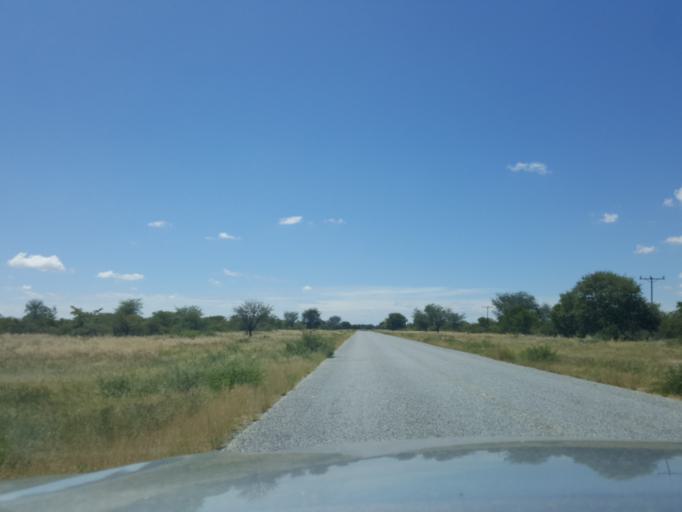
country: BW
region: Central
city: Nata
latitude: -20.1502
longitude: 25.7761
